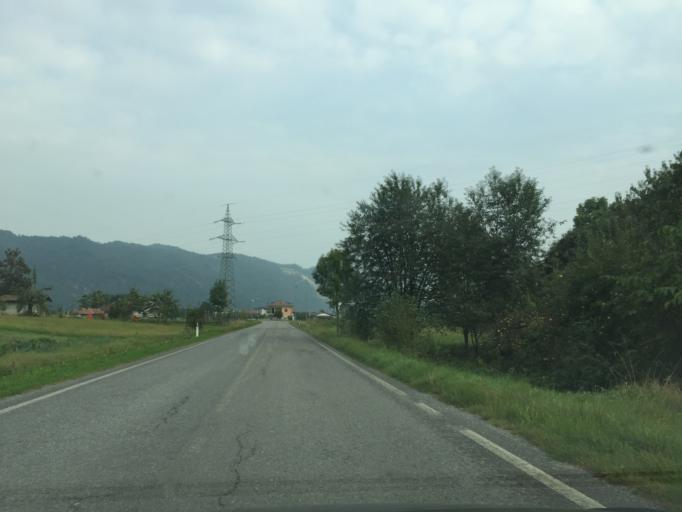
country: IT
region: Piedmont
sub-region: Provincia di Cuneo
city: Roccaforte Mondovi
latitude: 44.3070
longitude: 7.7457
